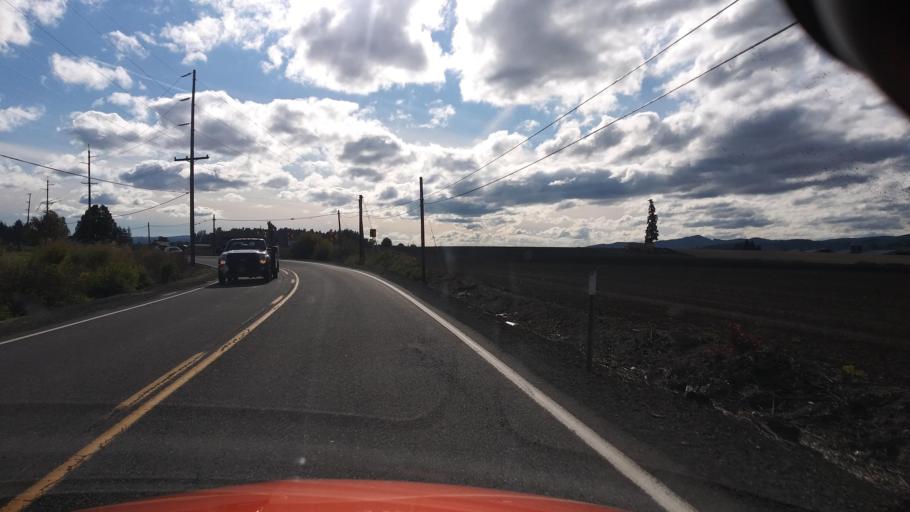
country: US
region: Oregon
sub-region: Washington County
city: Banks
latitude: 45.5708
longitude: -123.1093
